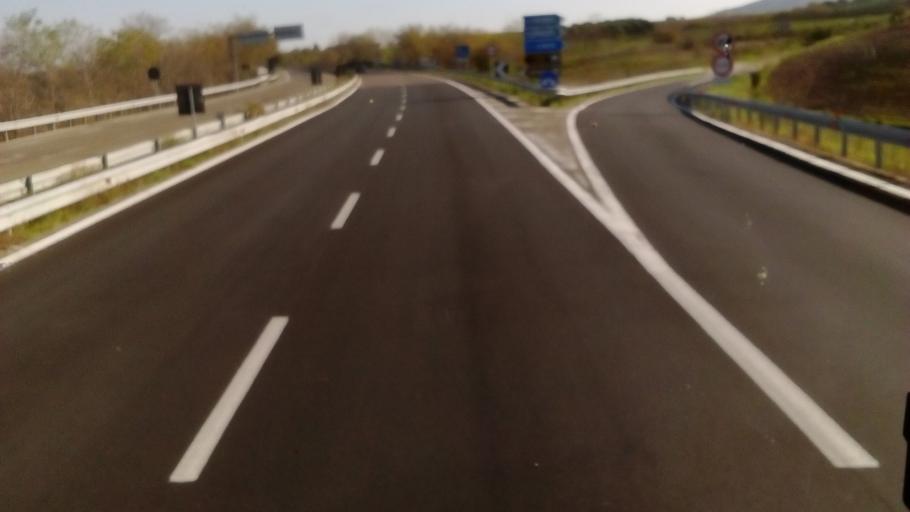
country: IT
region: Basilicate
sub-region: Provincia di Potenza
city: Zona 179
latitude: 41.0835
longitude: 15.6065
